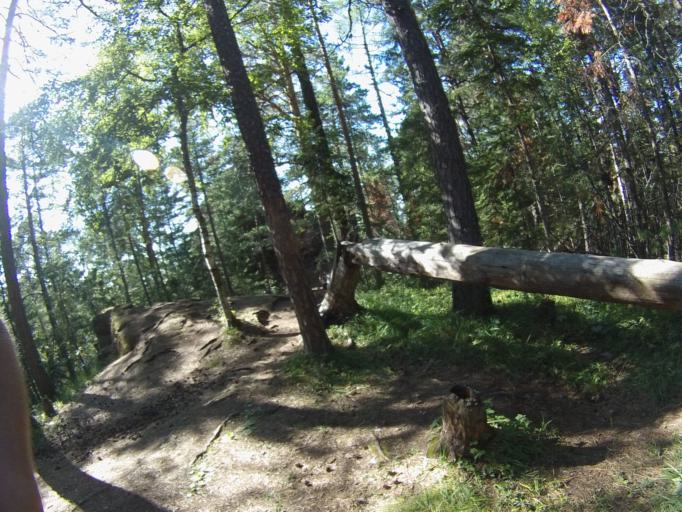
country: RU
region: Krasnoyarskiy
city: Krasnoyarsk
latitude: 55.9148
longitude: 92.7537
